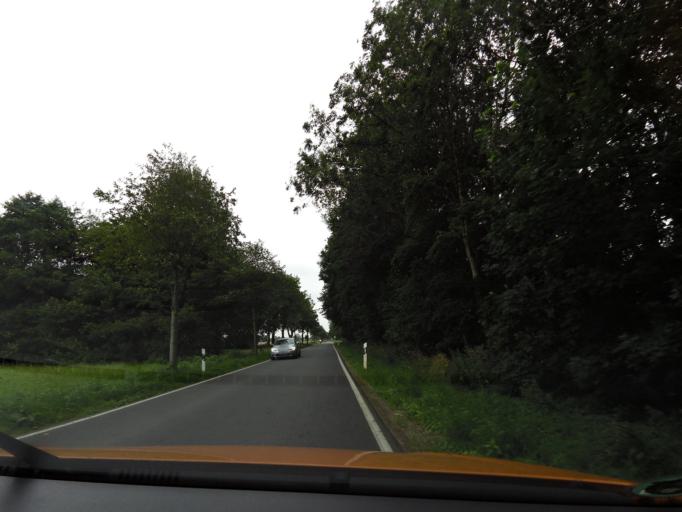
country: DE
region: Lower Saxony
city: Wirdum
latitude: 53.5102
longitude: 7.1465
